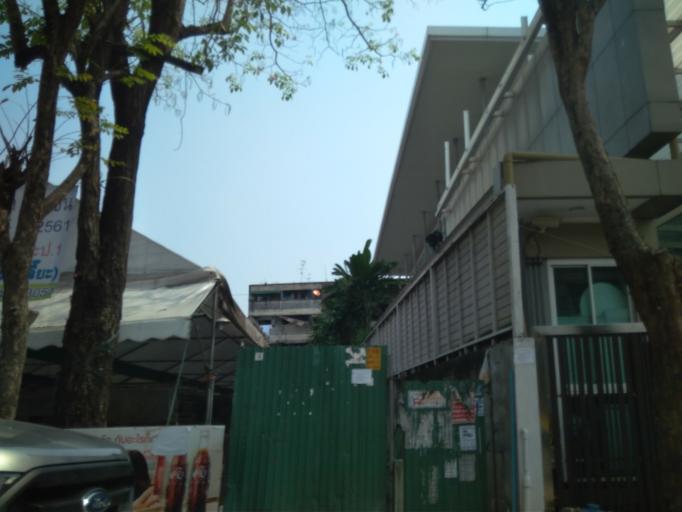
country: TH
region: Bangkok
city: Taling Chan
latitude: 13.7796
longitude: 100.4455
